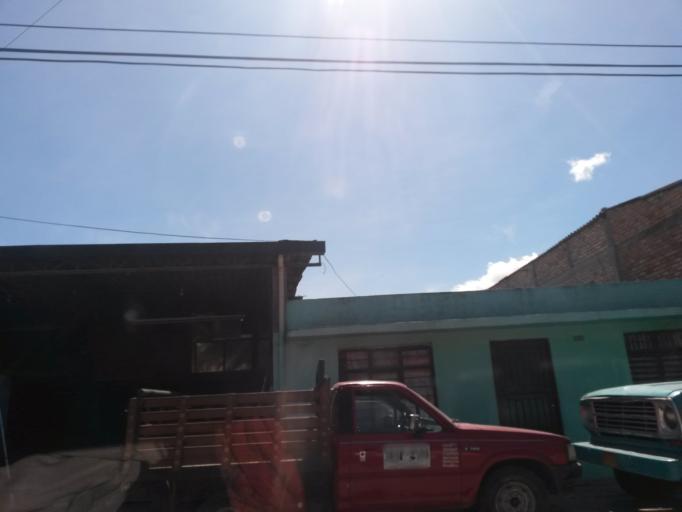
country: CO
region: Cauca
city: Popayan
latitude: 2.4521
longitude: -76.6290
